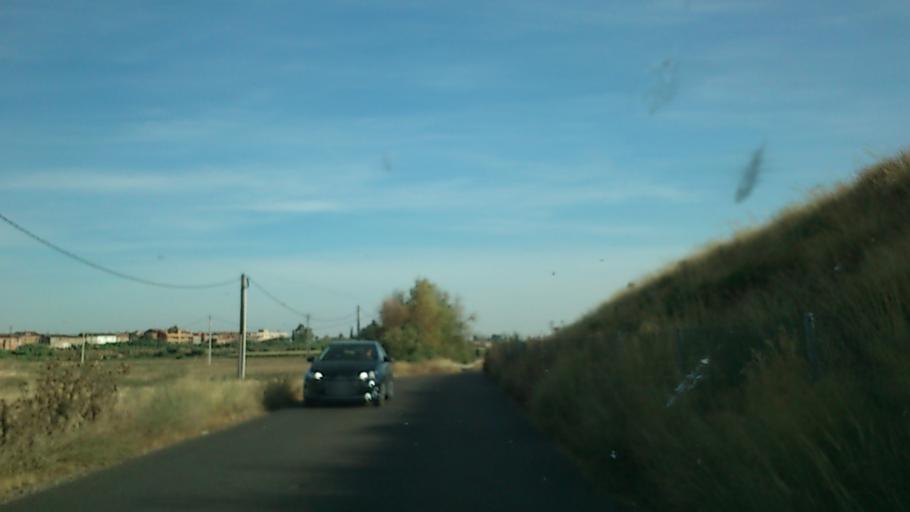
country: ES
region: Aragon
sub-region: Provincia de Zaragoza
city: Zaragoza
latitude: 41.6912
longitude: -0.8334
